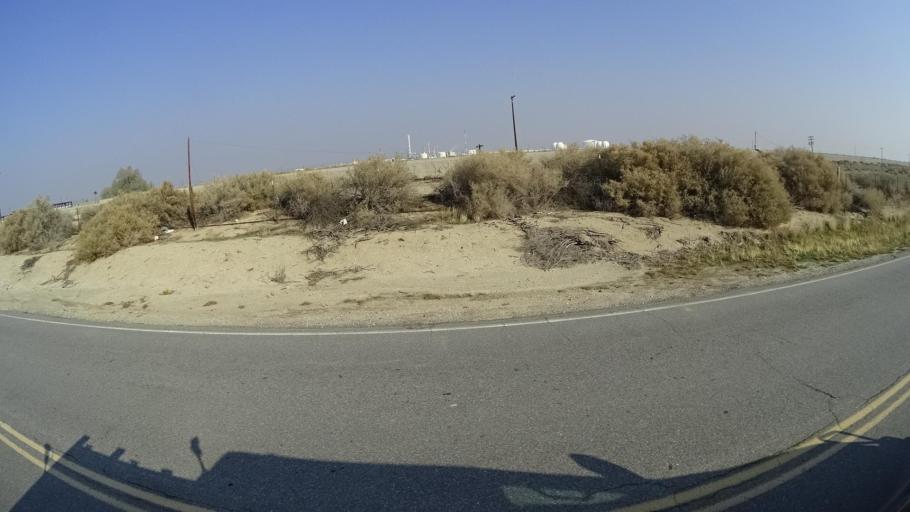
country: US
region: California
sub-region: Kern County
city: Ford City
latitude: 35.2736
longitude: -119.3199
